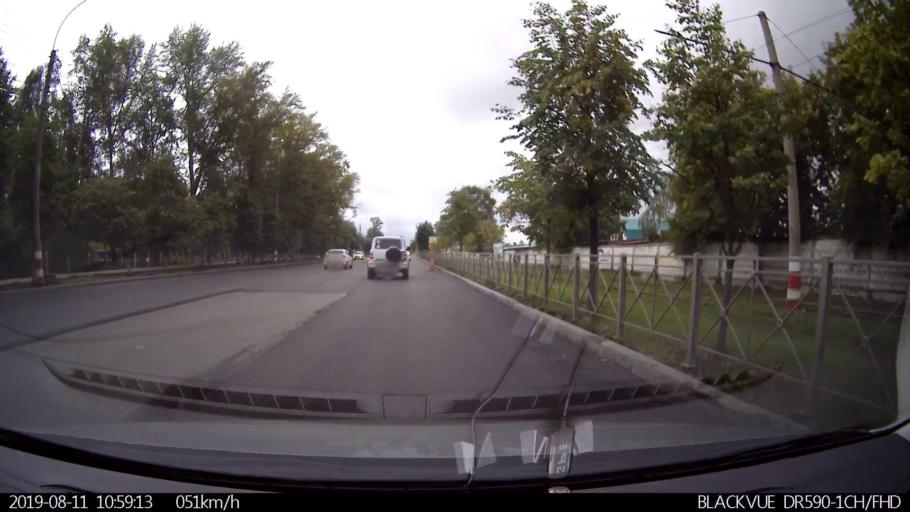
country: RU
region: Ulyanovsk
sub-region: Ulyanovskiy Rayon
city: Ulyanovsk
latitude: 54.2517
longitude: 48.3165
